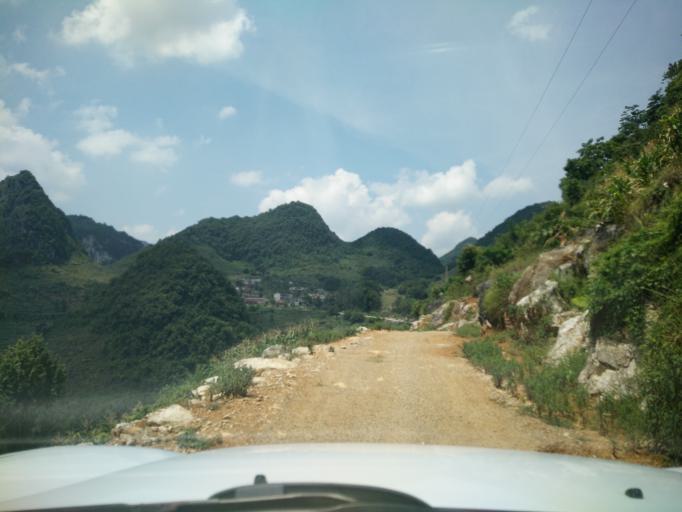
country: CN
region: Guangxi Zhuangzu Zizhiqu
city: Xinzhou
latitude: 25.0041
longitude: 105.7022
